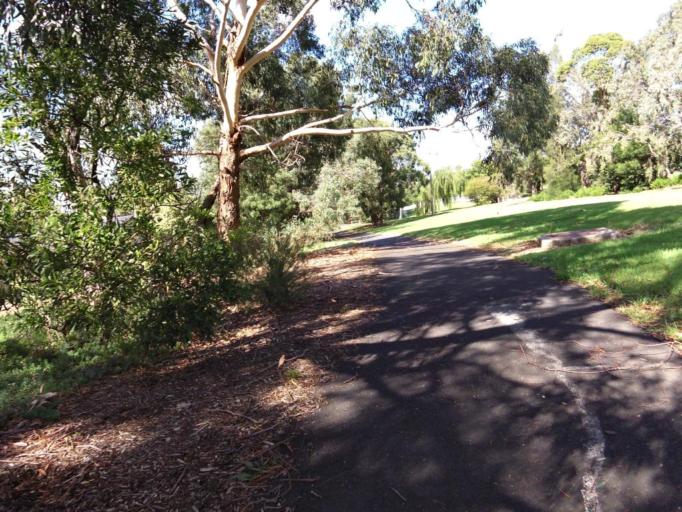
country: AU
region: Victoria
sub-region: Knox
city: Knoxfield
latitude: -37.8952
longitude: 145.2592
